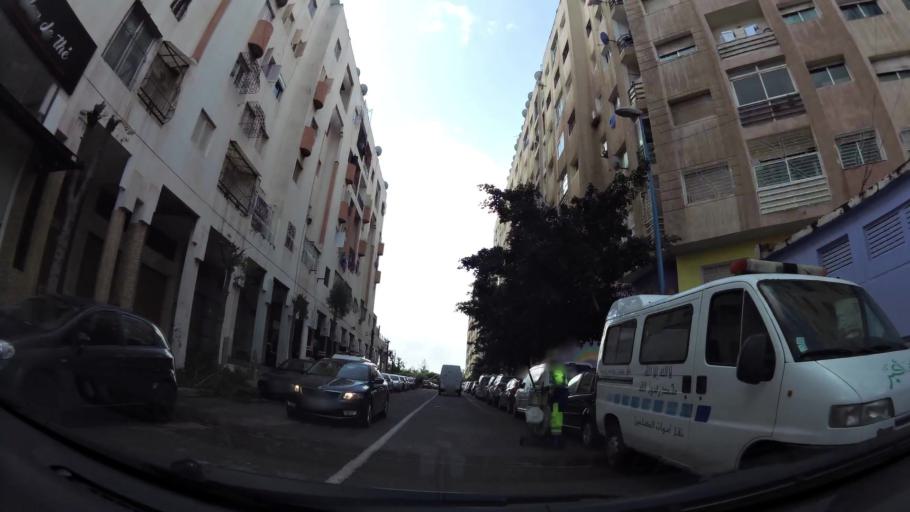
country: MA
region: Grand Casablanca
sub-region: Casablanca
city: Casablanca
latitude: 33.5546
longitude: -7.6291
